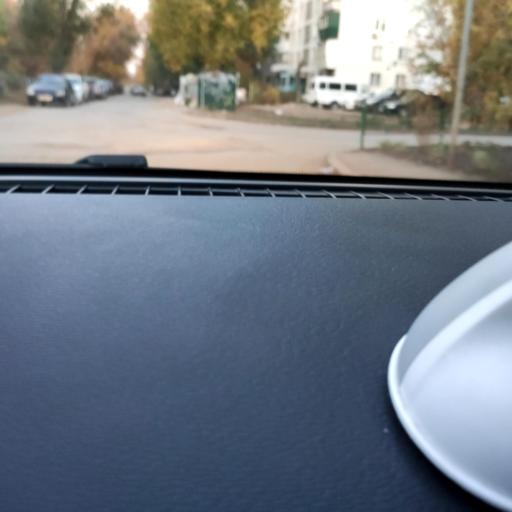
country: RU
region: Samara
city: Samara
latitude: 53.2359
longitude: 50.2064
